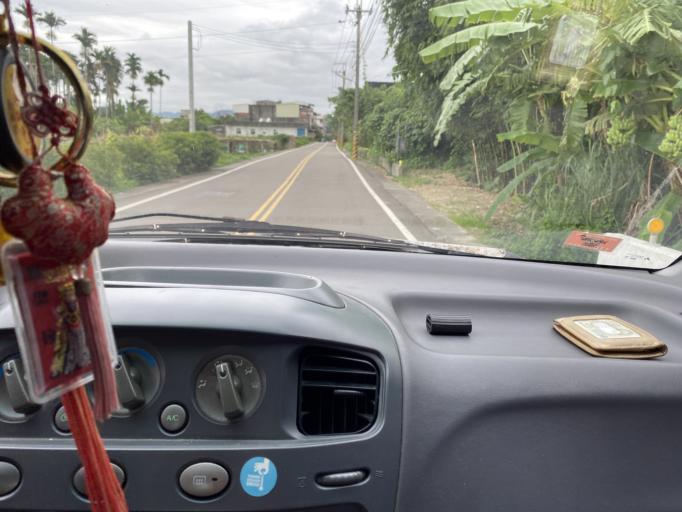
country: TW
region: Taiwan
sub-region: Hsinchu
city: Zhubei
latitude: 24.7197
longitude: 121.1127
